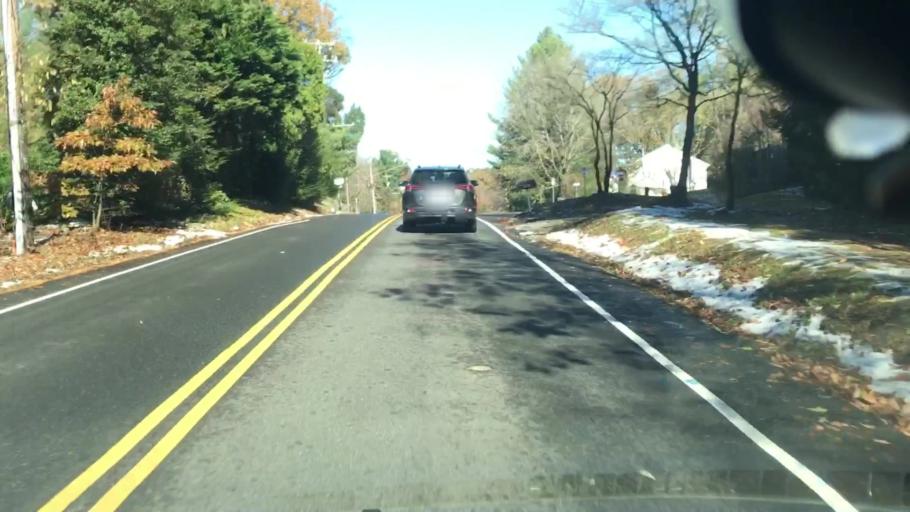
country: US
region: Virginia
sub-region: Fairfax County
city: Kings Park
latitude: 38.8289
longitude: -77.2393
